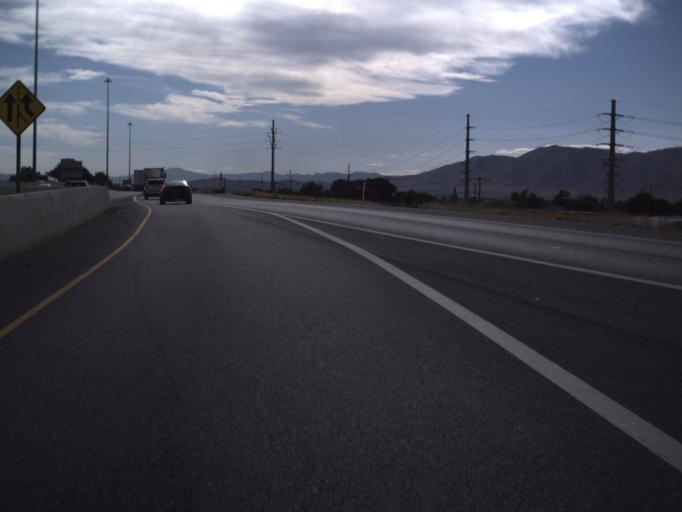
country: US
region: Utah
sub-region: Utah County
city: Spanish Fork
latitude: 40.1239
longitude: -111.6573
